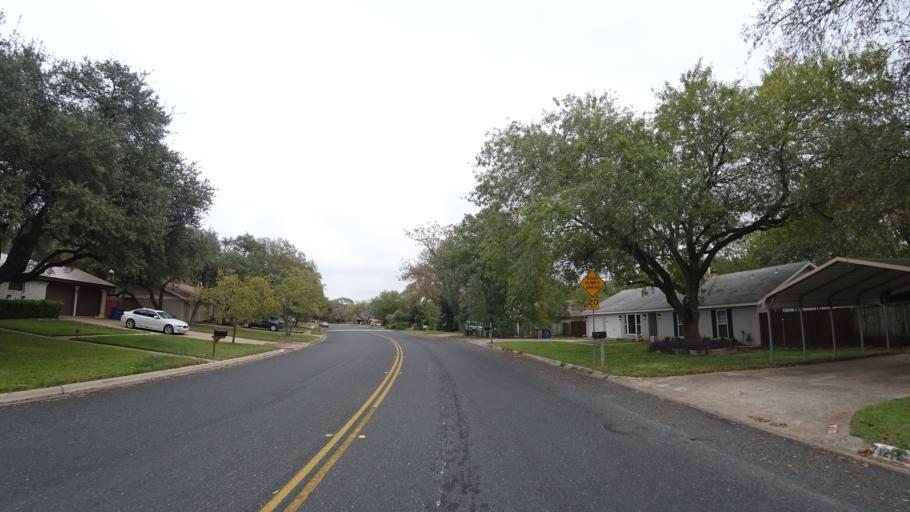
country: US
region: Texas
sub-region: Travis County
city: Barton Creek
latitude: 30.2367
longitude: -97.8859
